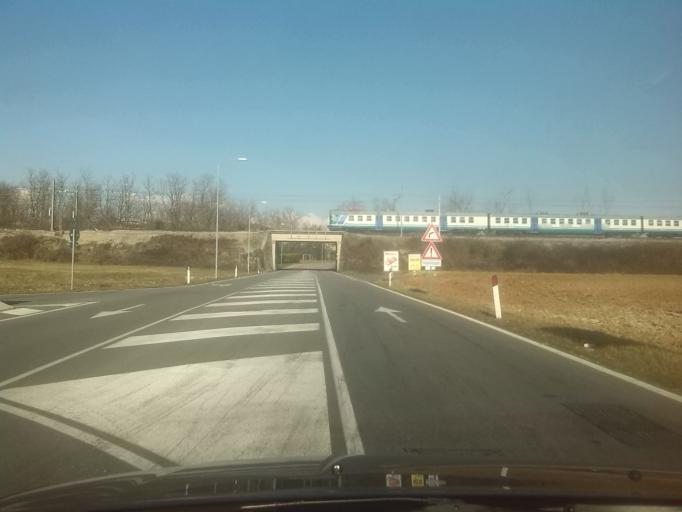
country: IT
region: Friuli Venezia Giulia
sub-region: Provincia di Udine
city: Manzano
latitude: 45.9831
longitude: 13.3818
